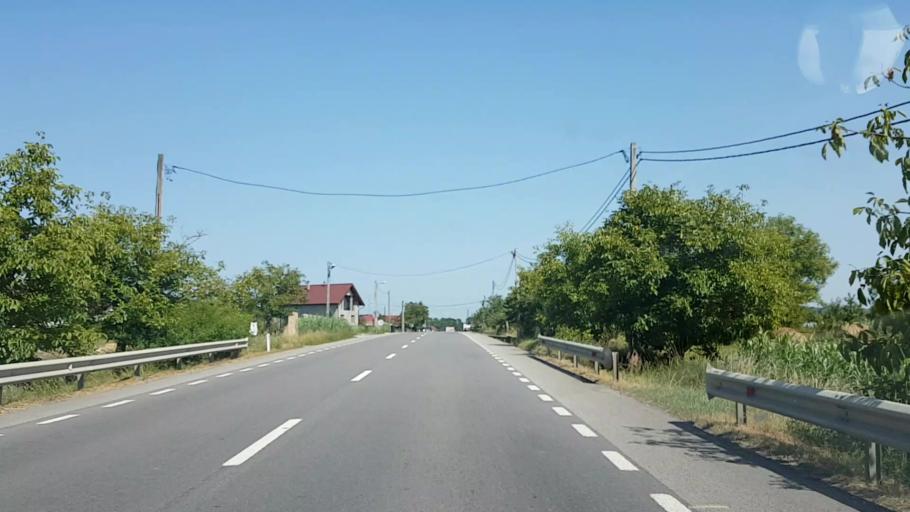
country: RO
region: Bistrita-Nasaud
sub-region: Comuna Uriu
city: Cristestii Ciceului
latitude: 47.1832
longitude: 24.1318
